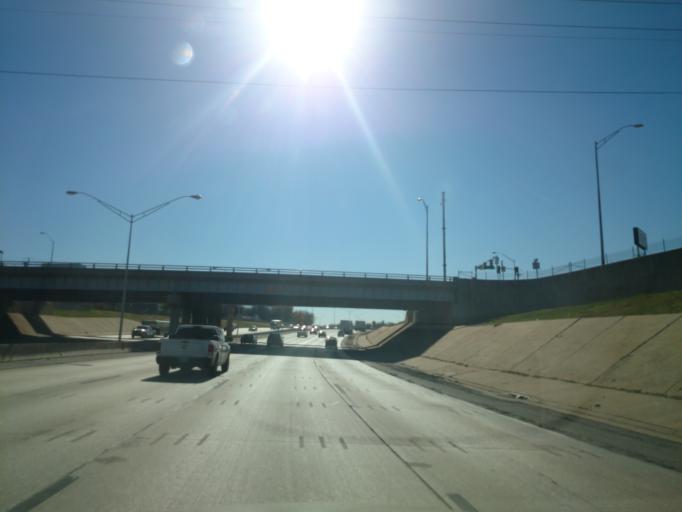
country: US
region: Oklahoma
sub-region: Oklahoma County
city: Warr Acres
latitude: 35.4940
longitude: -97.5789
